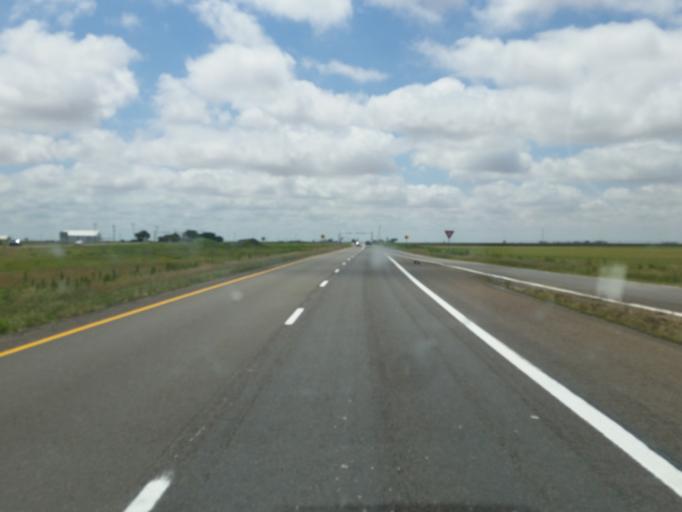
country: US
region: Texas
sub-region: Lubbock County
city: Slaton
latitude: 33.4173
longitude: -101.6383
